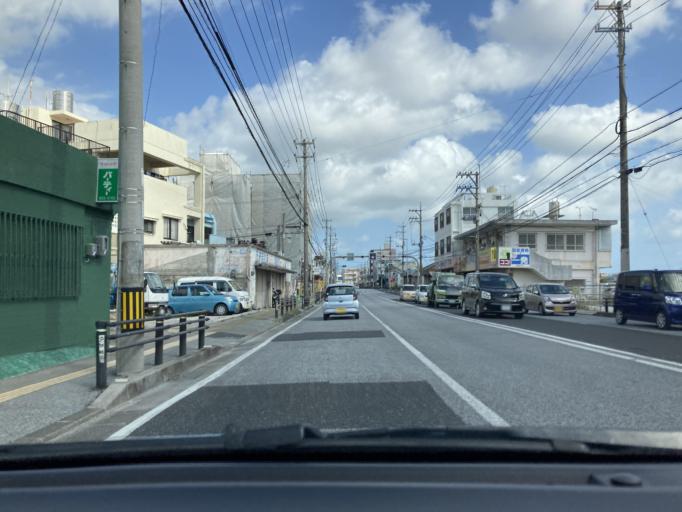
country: JP
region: Okinawa
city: Tomigusuku
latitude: 26.1965
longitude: 127.6982
